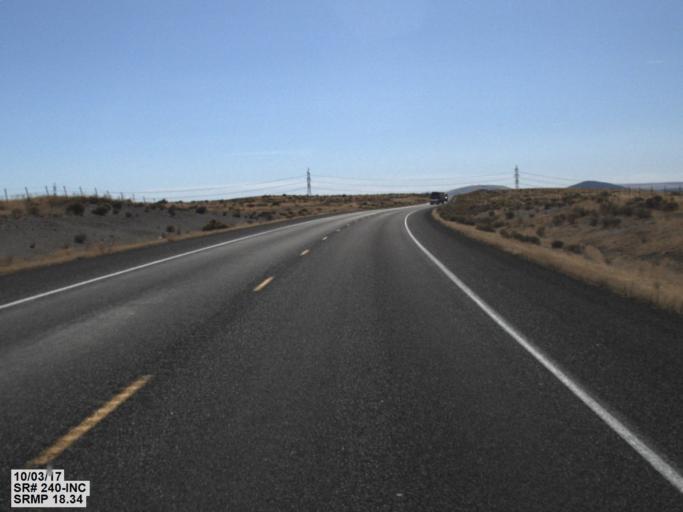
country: US
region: Washington
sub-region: Benton County
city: West Richland
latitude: 46.4075
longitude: -119.4496
